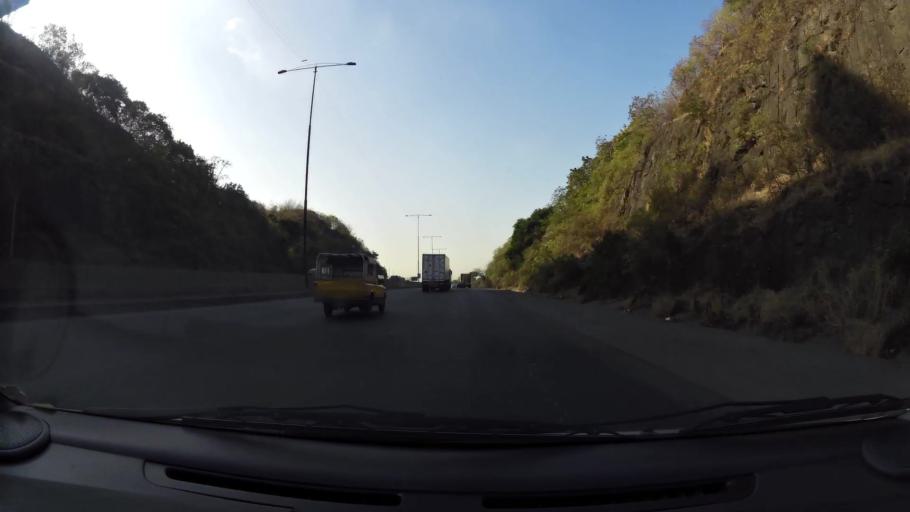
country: EC
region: Guayas
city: Santa Lucia
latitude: -2.1537
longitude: -79.9470
